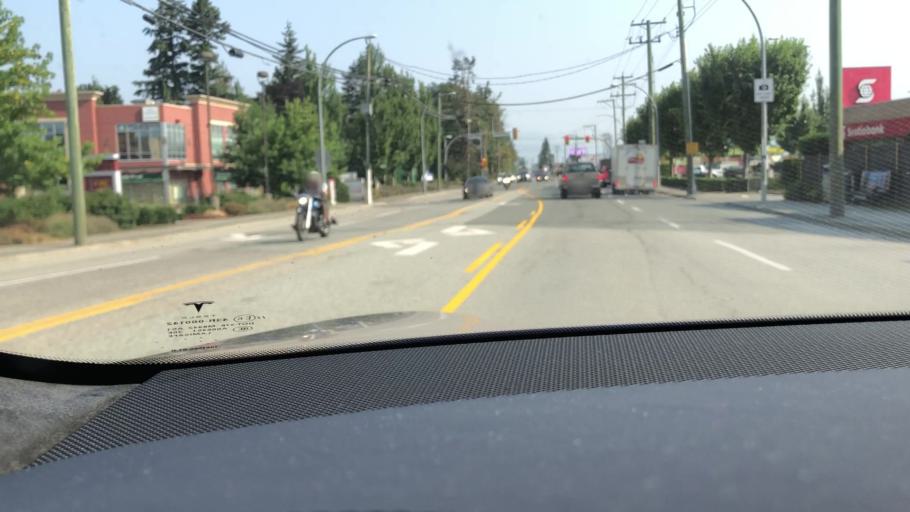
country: CA
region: British Columbia
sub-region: Fraser Valley Regional District
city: Chilliwack
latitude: 49.1102
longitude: -121.9582
